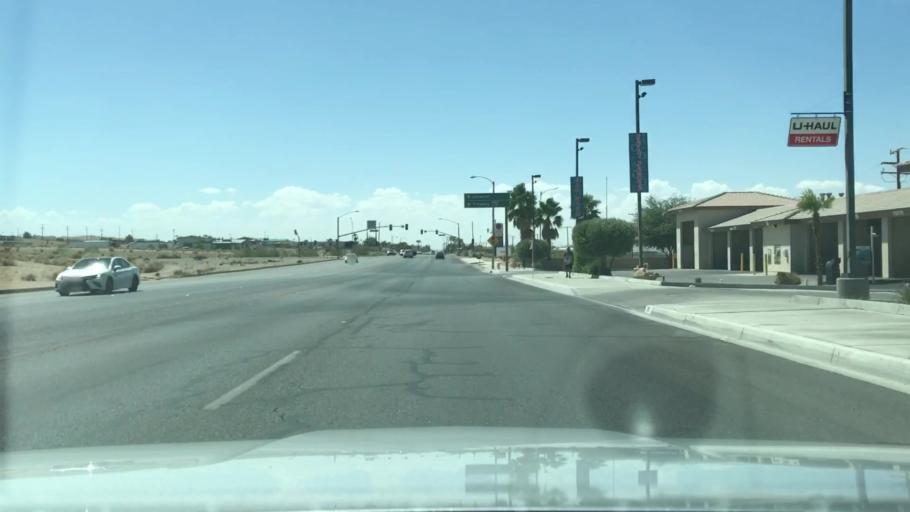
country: US
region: California
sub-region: San Bernardino County
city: Barstow Heights
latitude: 34.8922
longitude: -117.0553
